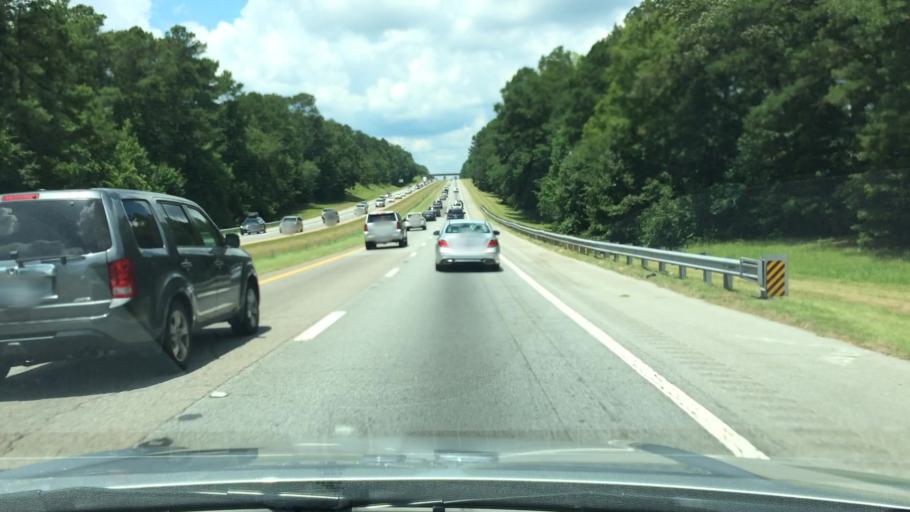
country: US
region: South Carolina
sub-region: Newberry County
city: Prosperity
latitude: 34.2476
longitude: -81.4791
